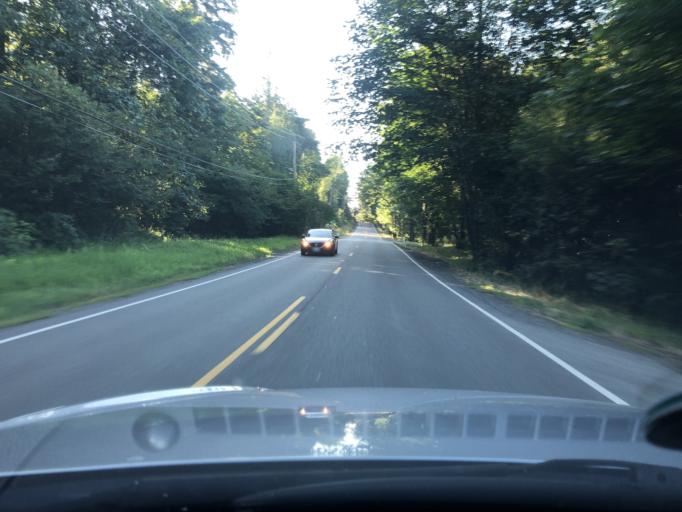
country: US
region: Washington
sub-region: Pierce County
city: Bonney Lake
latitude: 47.2440
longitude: -122.1491
